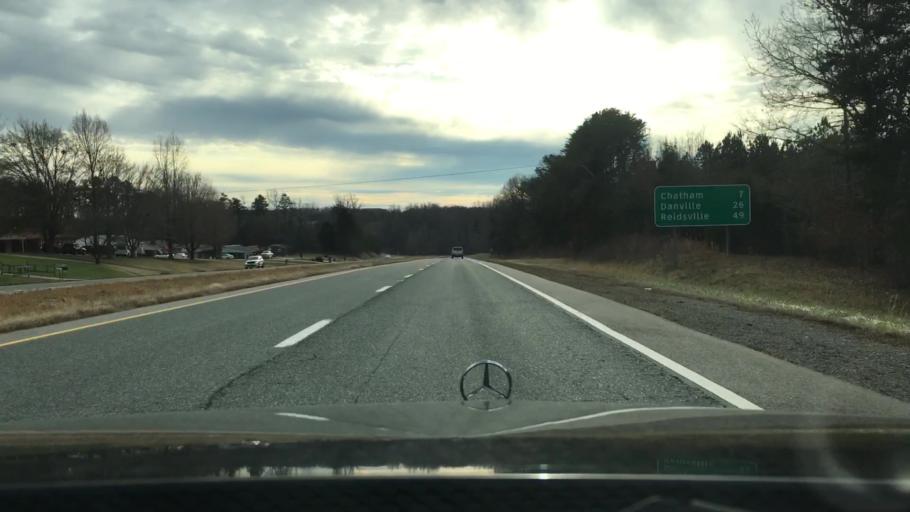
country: US
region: Virginia
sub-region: Pittsylvania County
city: Gretna
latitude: 36.9170
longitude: -79.3852
